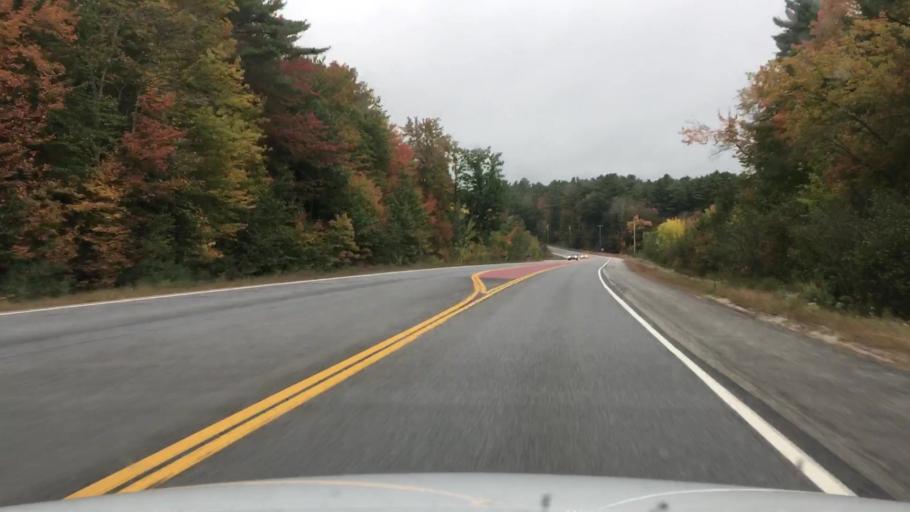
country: US
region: Maine
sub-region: Cumberland County
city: New Gloucester
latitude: 43.9687
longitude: -70.3628
